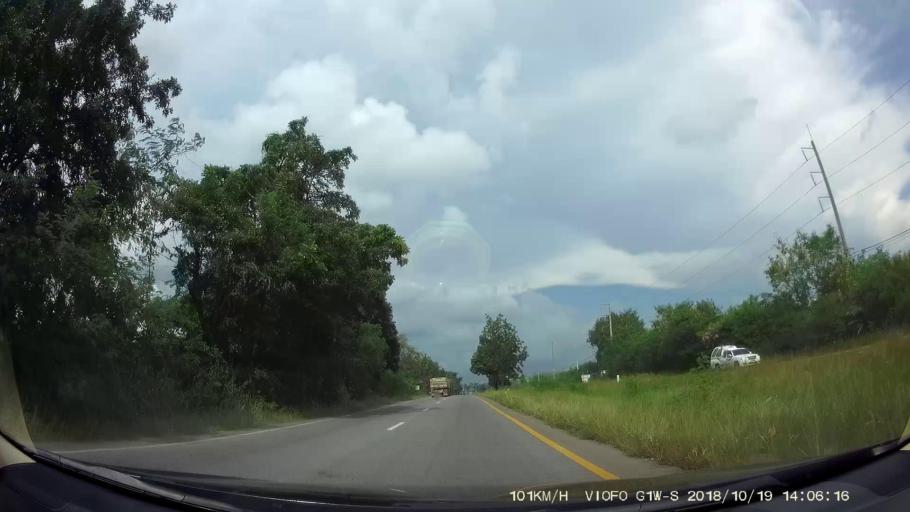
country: TH
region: Chaiyaphum
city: Chaiyaphum
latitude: 15.8849
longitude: 102.1026
